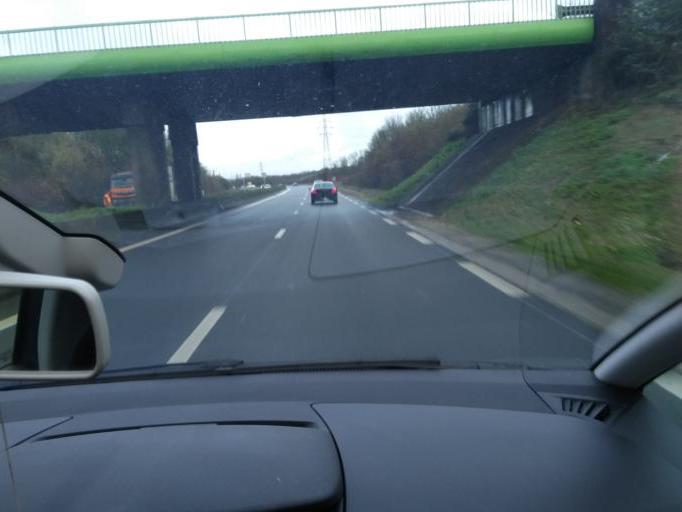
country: FR
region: Picardie
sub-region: Departement de la Somme
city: Rivery
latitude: 49.9132
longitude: 2.3427
